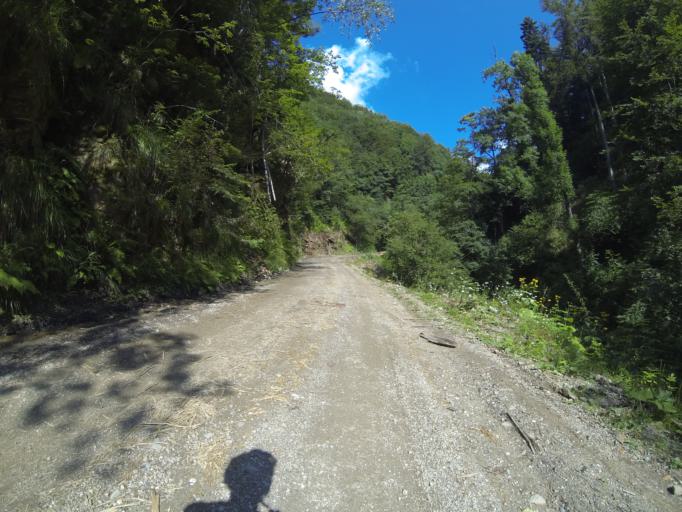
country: RO
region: Valcea
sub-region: Comuna Costesti
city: Bistrita
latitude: 45.2489
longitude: 23.9935
